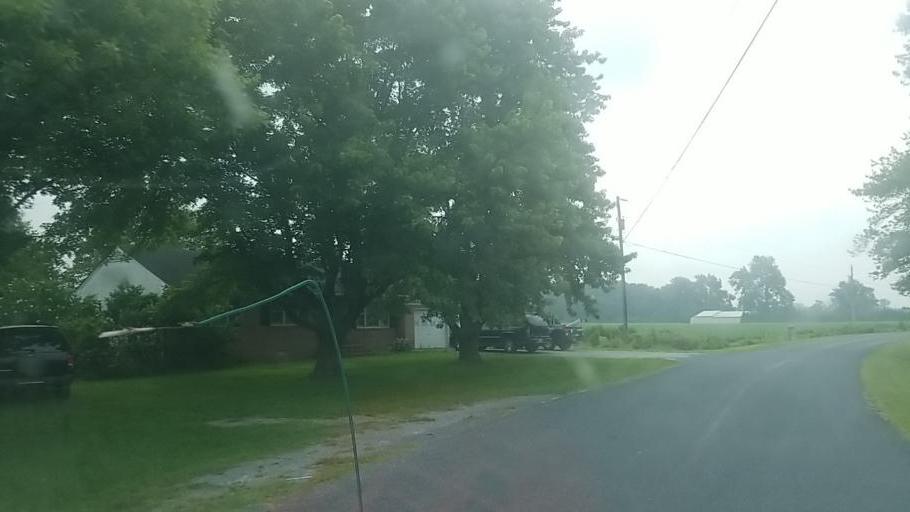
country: US
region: Maryland
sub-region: Wicomico County
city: Pittsville
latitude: 38.4478
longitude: -75.3489
